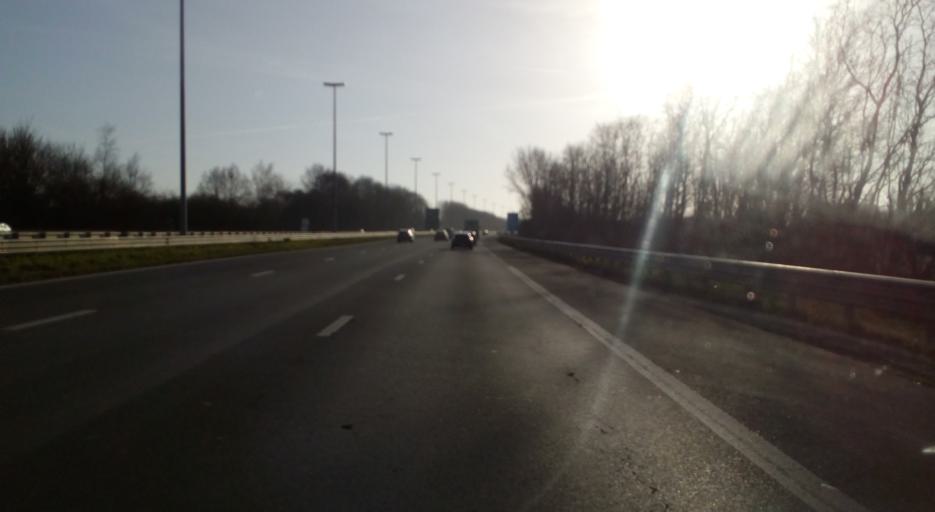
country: BE
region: Wallonia
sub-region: Province du Brabant Wallon
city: Braine-le-Chateau
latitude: 50.6761
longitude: 4.3094
